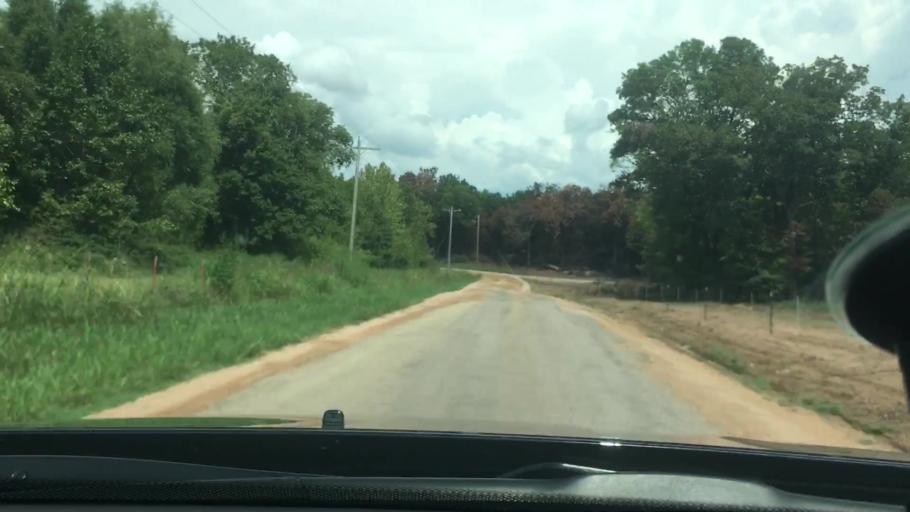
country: US
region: Oklahoma
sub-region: Carter County
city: Dickson
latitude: 34.2392
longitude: -96.9157
